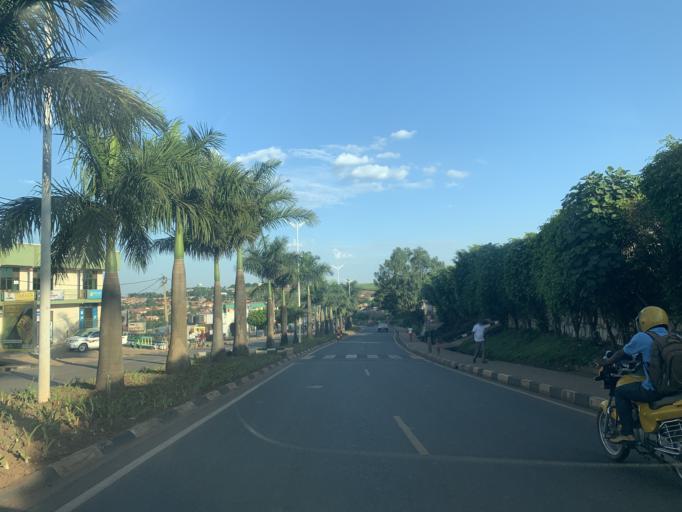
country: RW
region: Kigali
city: Kigali
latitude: -1.9615
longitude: 30.1221
